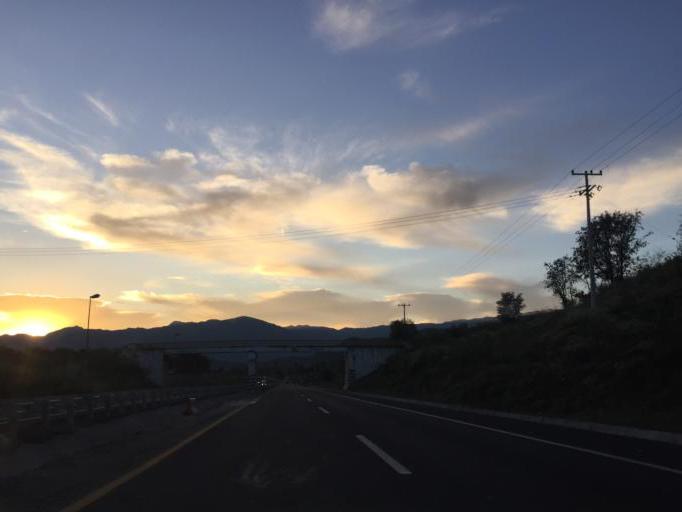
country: MX
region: Veracruz
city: Maltrata
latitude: 18.8308
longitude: -97.2569
